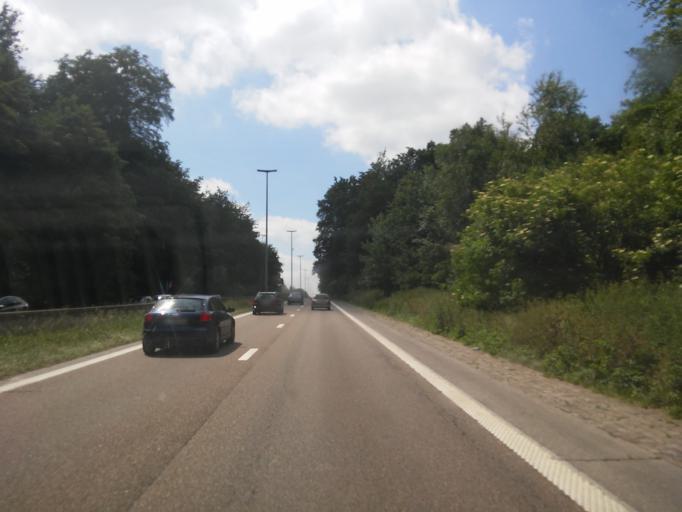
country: BE
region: Flanders
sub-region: Provincie Vlaams-Brabant
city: Hoeilaart
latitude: 50.7935
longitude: 4.4600
